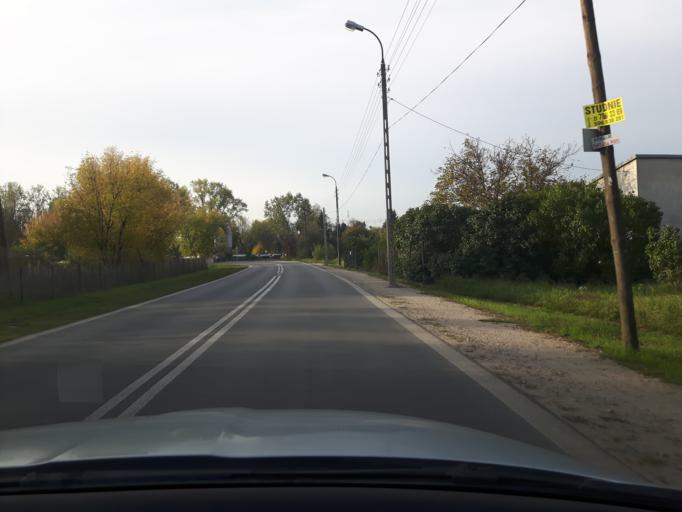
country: PL
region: Masovian Voivodeship
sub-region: Powiat wolominski
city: Zabki
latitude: 52.2758
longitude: 21.0879
